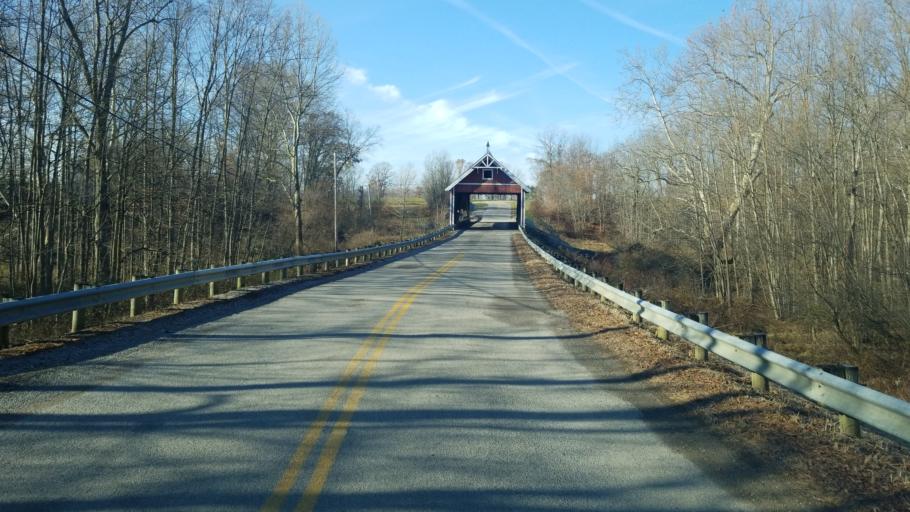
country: US
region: Ohio
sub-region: Ashtabula County
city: Jefferson
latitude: 41.7373
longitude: -80.7304
